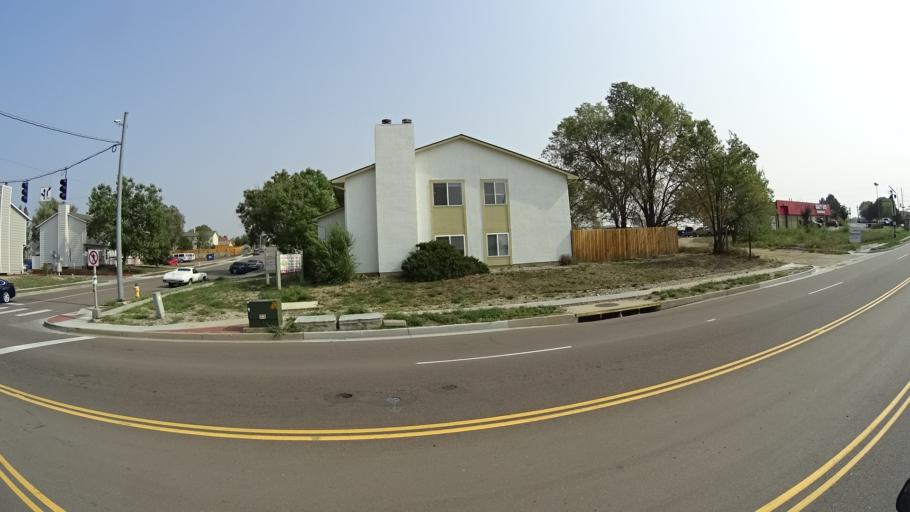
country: US
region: Colorado
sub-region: El Paso County
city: Stratmoor
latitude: 38.8055
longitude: -104.7607
